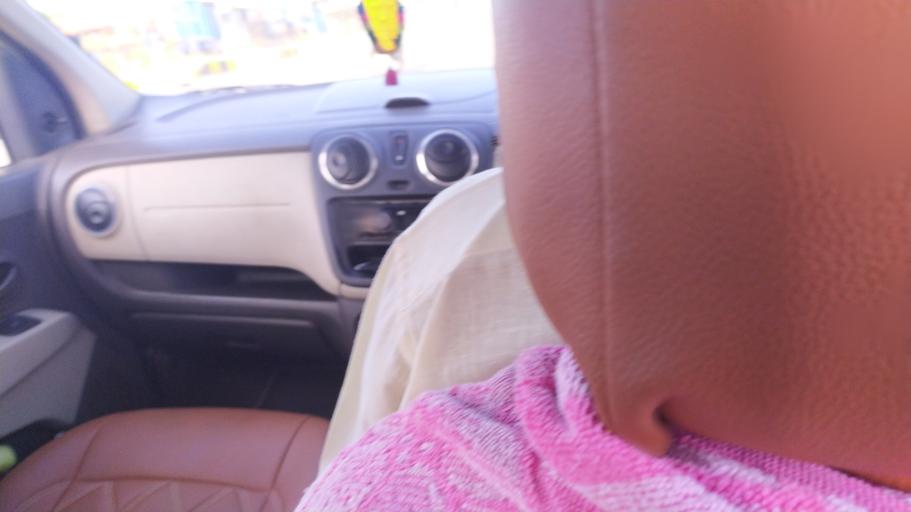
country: IN
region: Telangana
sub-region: Rangareddi
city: Balapur
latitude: 17.3144
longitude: 78.4440
